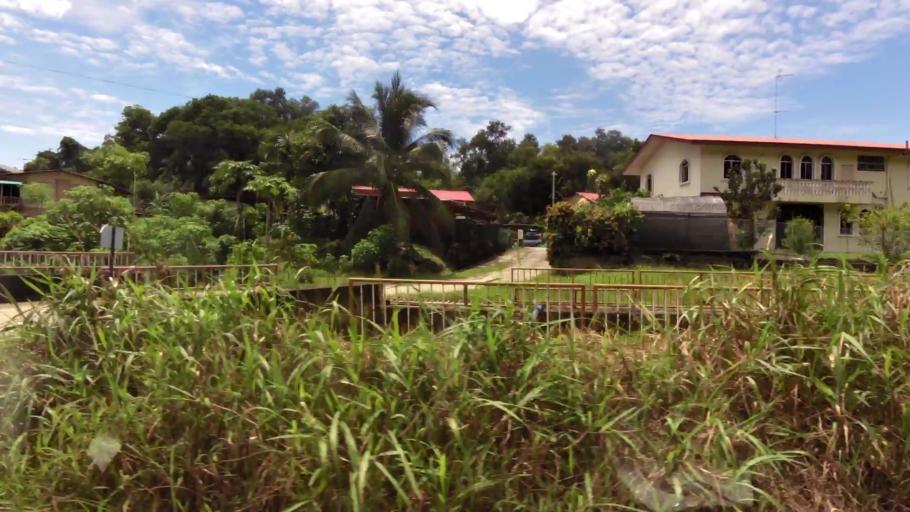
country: BN
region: Brunei and Muara
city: Bandar Seri Begawan
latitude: 4.9923
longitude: 115.0207
